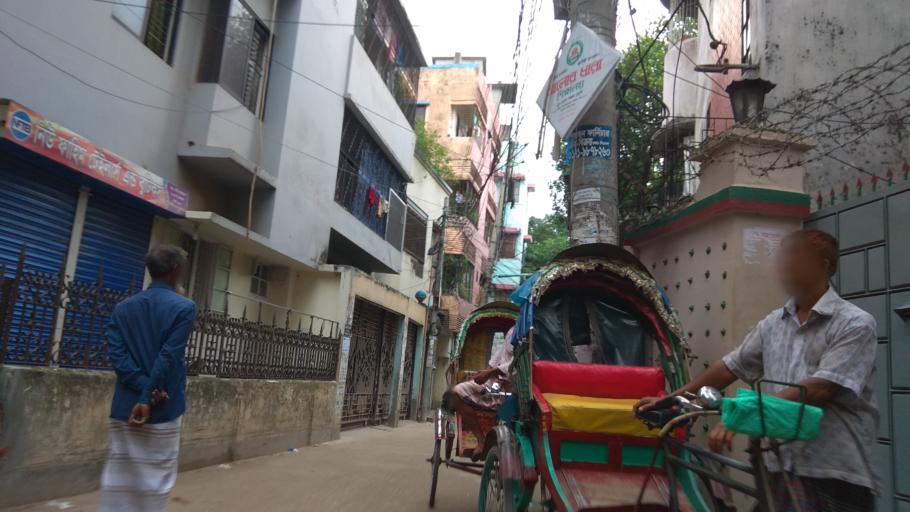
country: BD
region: Dhaka
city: Azimpur
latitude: 23.7965
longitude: 90.3800
